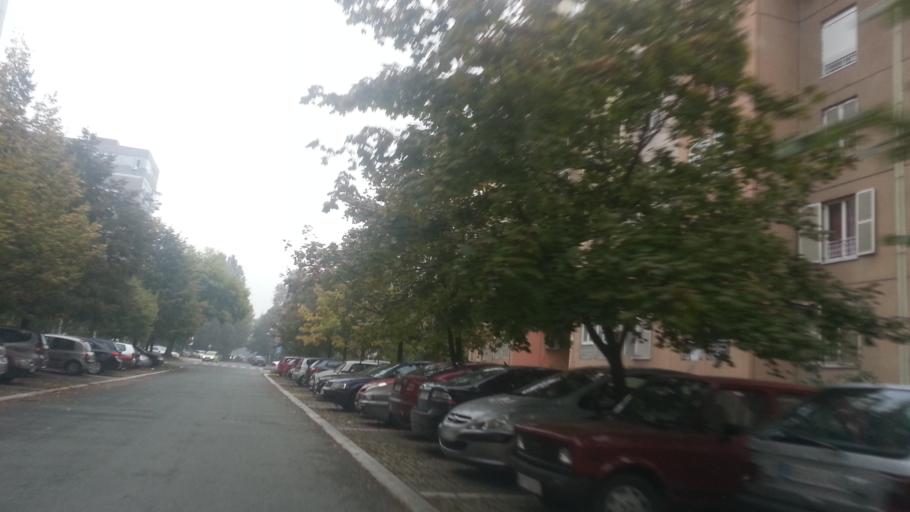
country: RS
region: Central Serbia
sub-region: Belgrade
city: Zemun
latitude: 44.8345
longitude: 20.4118
